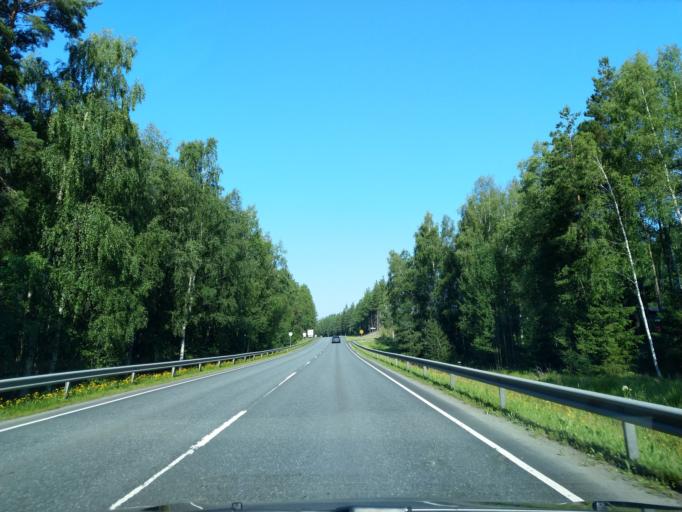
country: FI
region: Haeme
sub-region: Forssa
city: Humppila
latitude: 60.9705
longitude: 23.2755
